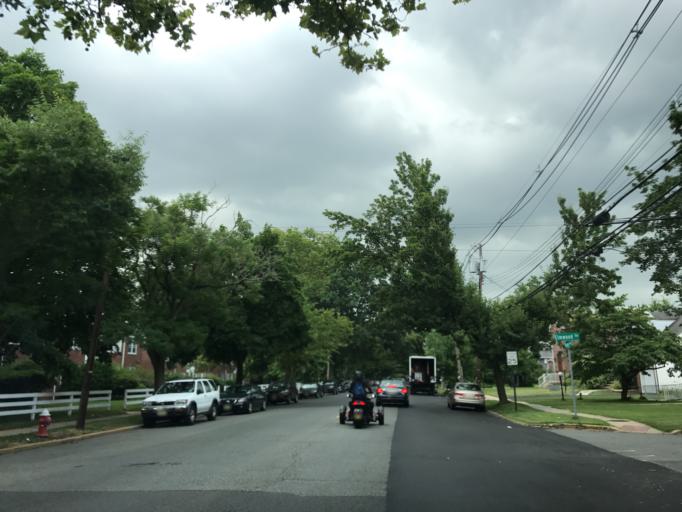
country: US
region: New Jersey
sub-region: Union County
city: Winfield
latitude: 40.6435
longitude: -74.2727
